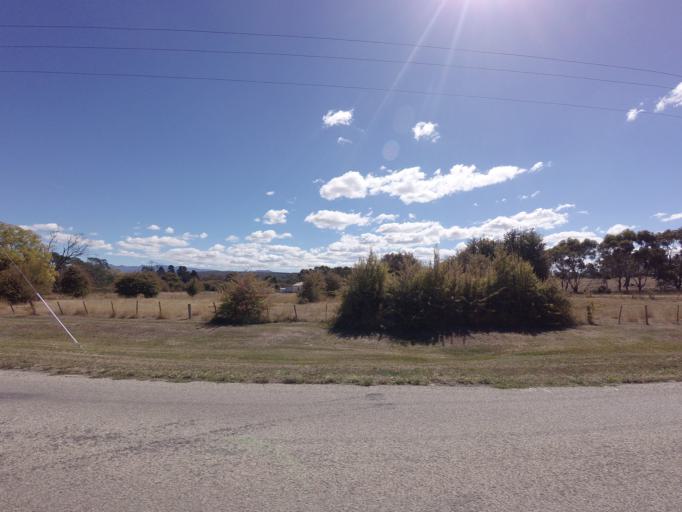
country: AU
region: Tasmania
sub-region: Break O'Day
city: St Helens
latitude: -41.6349
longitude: 147.9814
